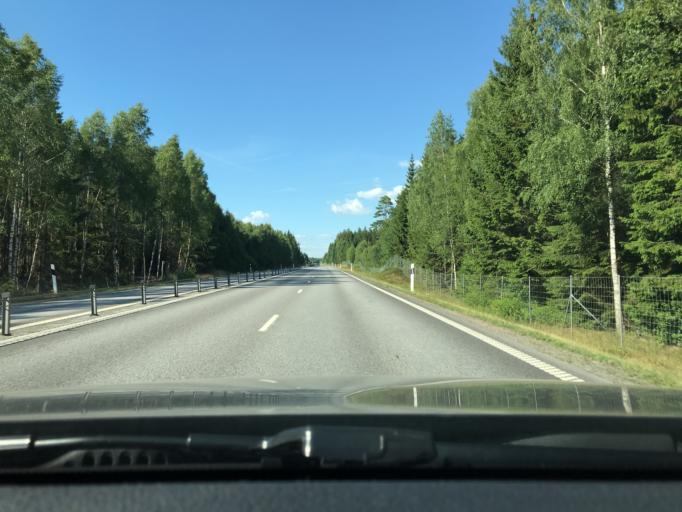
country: SE
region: Skane
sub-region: Osby Kommun
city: Osby
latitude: 56.4194
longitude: 14.0523
